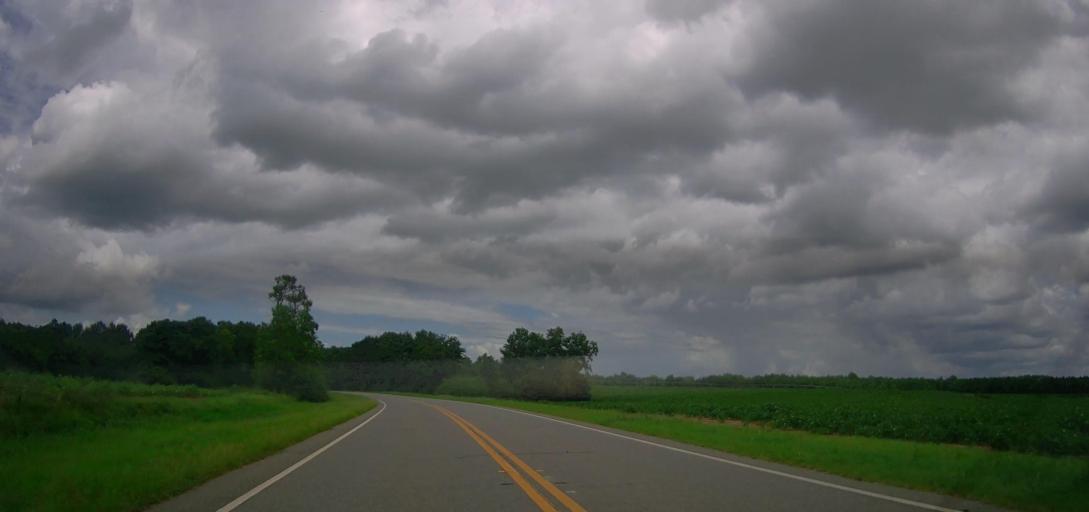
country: US
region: Georgia
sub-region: Wilcox County
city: Rochelle
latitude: 31.9582
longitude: -83.5411
